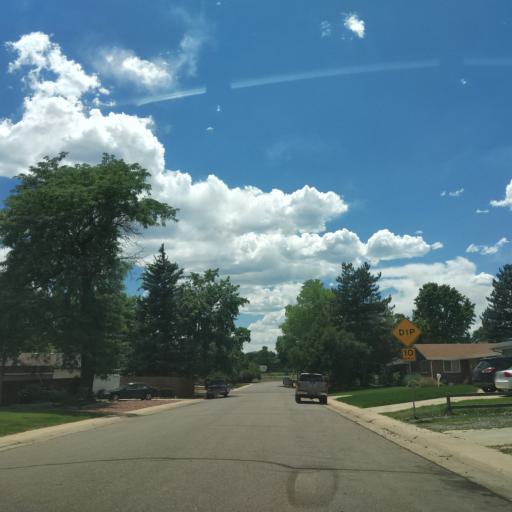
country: US
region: Colorado
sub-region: Jefferson County
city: Lakewood
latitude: 39.6842
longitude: -105.0940
